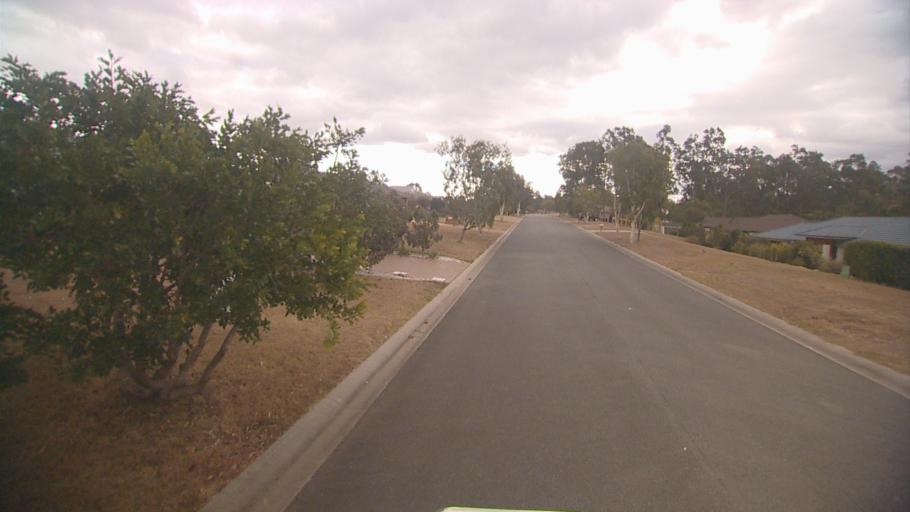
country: AU
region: Queensland
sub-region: Logan
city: Cedar Vale
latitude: -27.8755
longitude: 153.0760
